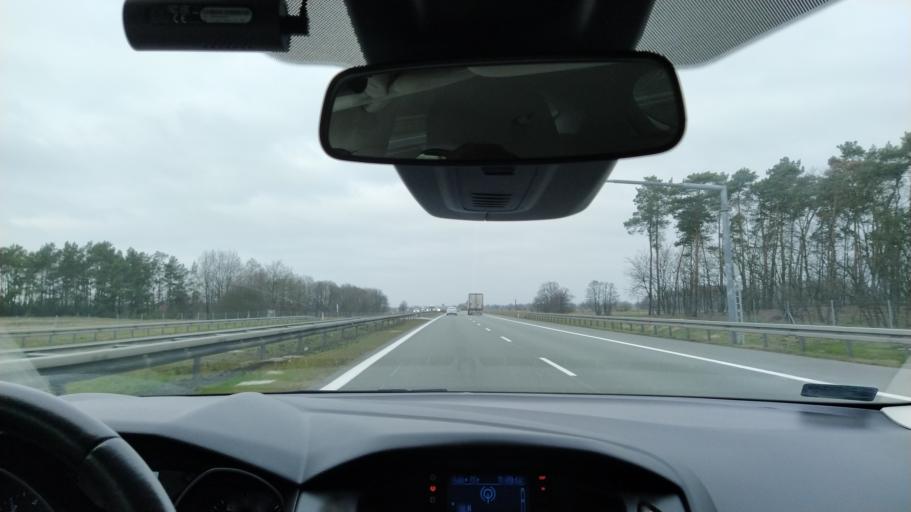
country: PL
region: Greater Poland Voivodeship
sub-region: Powiat koninski
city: Rzgow Pierwszy
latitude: 52.1884
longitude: 18.0817
